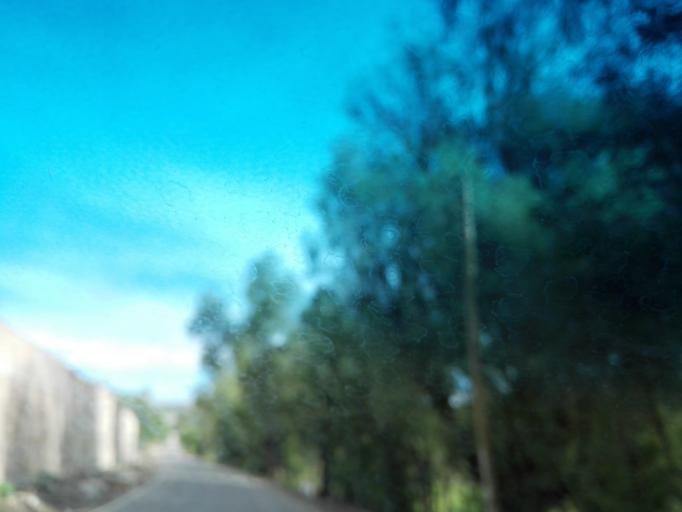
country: PE
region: Ayacucho
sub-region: Provincia de Huamanga
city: Pacaycasa
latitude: -13.0781
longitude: -74.2323
